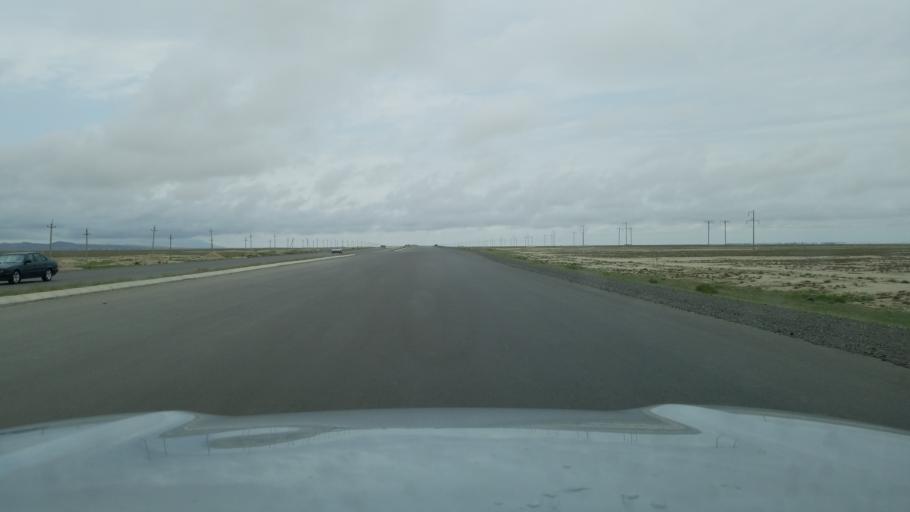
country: TM
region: Balkan
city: Serdar
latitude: 39.1086
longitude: 55.9278
